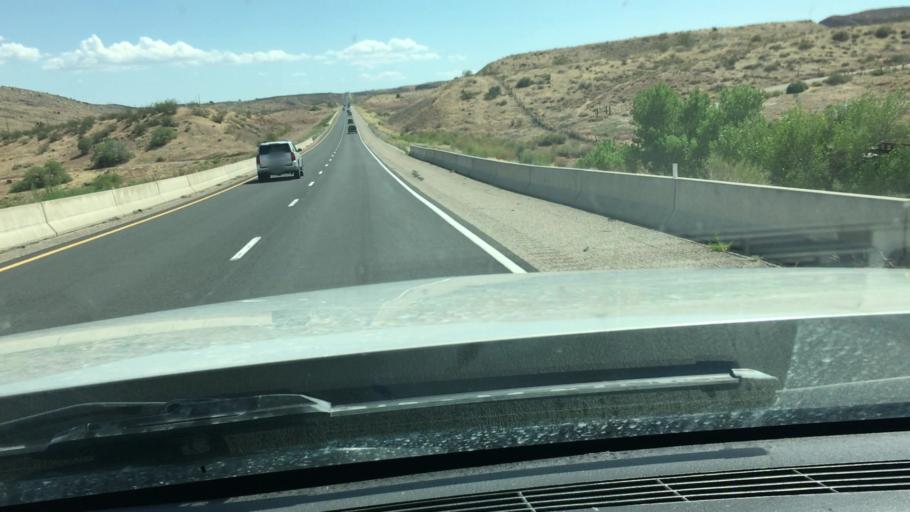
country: US
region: Utah
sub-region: Washington County
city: Hurricane
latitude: 37.2075
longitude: -113.3959
